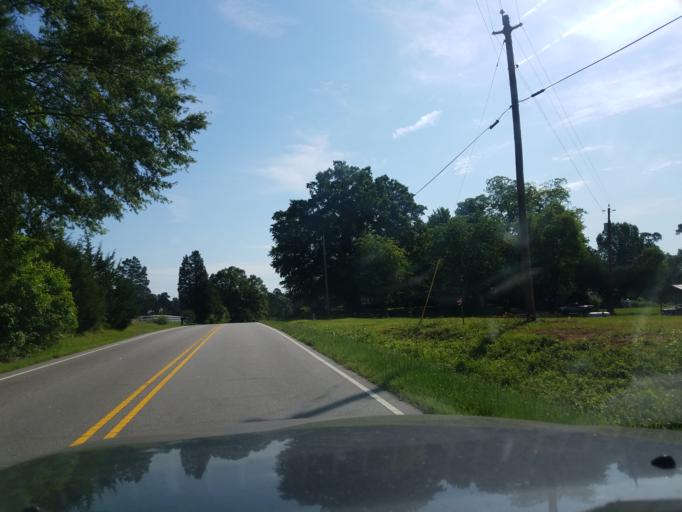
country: US
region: North Carolina
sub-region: Granville County
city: Butner
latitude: 36.1904
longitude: -78.7368
